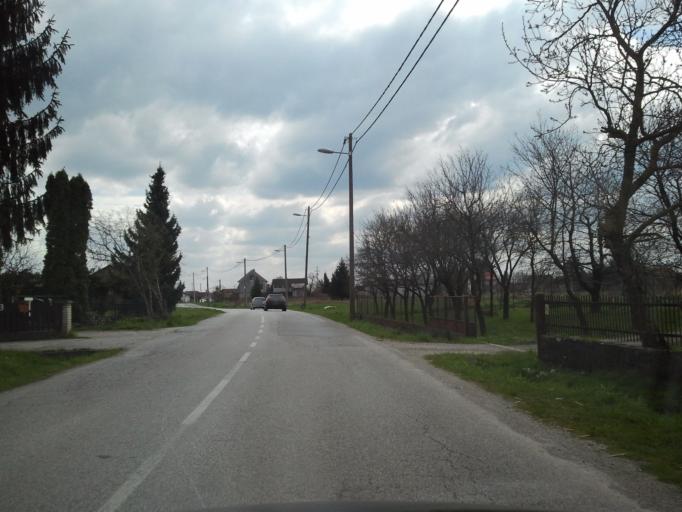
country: HR
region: Grad Zagreb
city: Lucko
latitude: 45.7529
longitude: 15.8439
